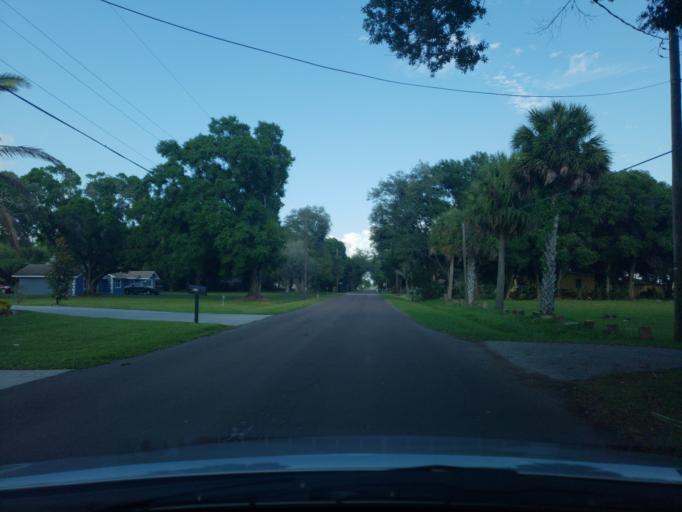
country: US
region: Florida
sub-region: Hillsborough County
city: Palm River-Clair Mel
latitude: 27.9155
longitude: -82.3863
